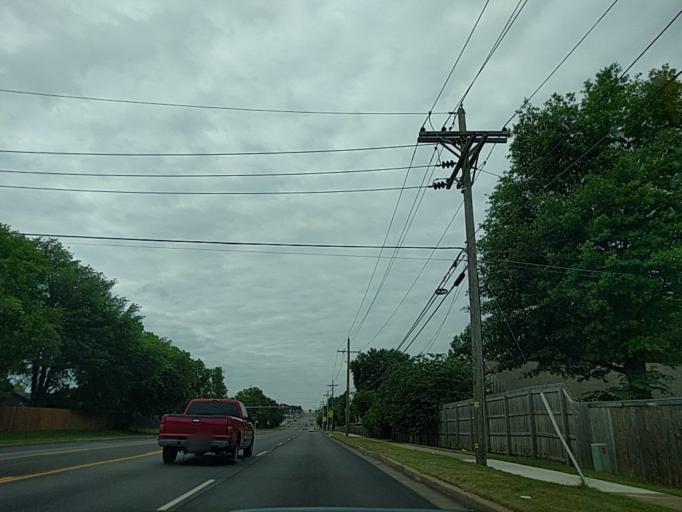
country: US
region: Oklahoma
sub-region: Tulsa County
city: Jenks
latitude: 36.0829
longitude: -95.9044
